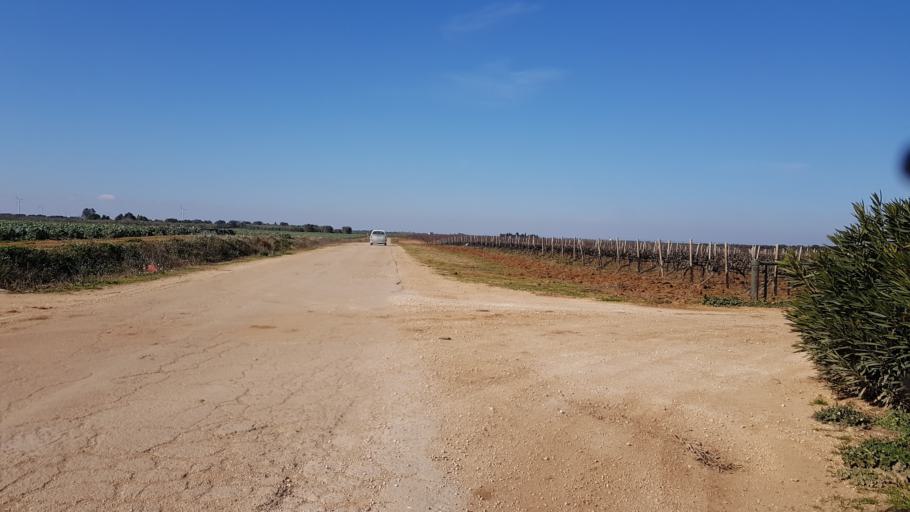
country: IT
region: Apulia
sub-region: Provincia di Brindisi
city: Mesagne
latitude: 40.6210
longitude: 17.8092
